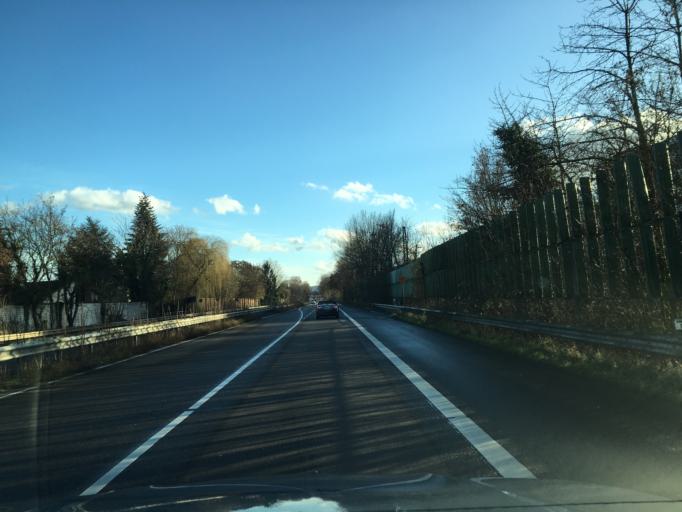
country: DE
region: North Rhine-Westphalia
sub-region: Regierungsbezirk Koln
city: Konigswinter
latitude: 50.6578
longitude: 7.1923
